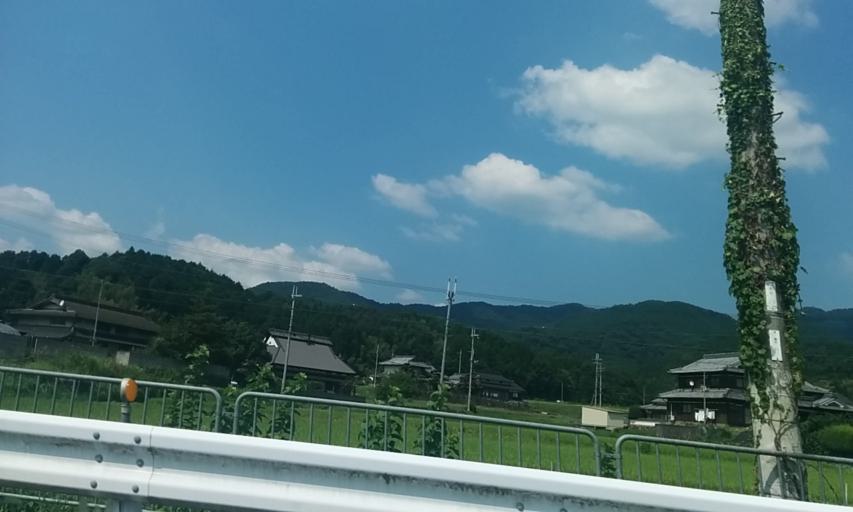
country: JP
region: Kyoto
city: Fukuchiyama
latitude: 35.3142
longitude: 135.1256
